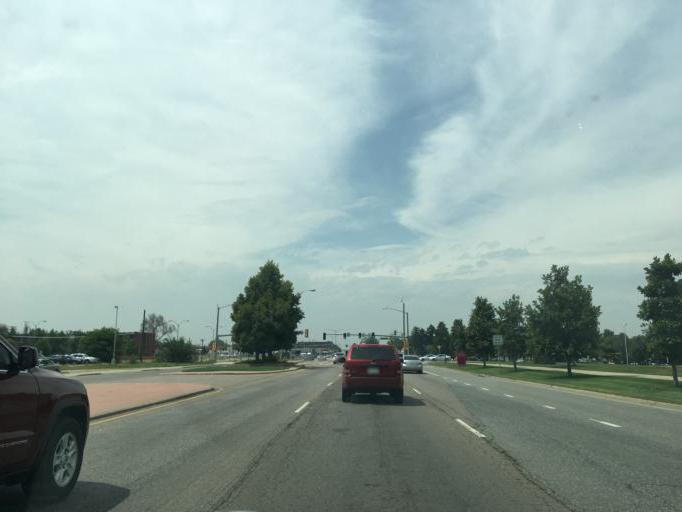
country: US
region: Colorado
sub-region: Adams County
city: Aurora
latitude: 39.7403
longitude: -104.8430
